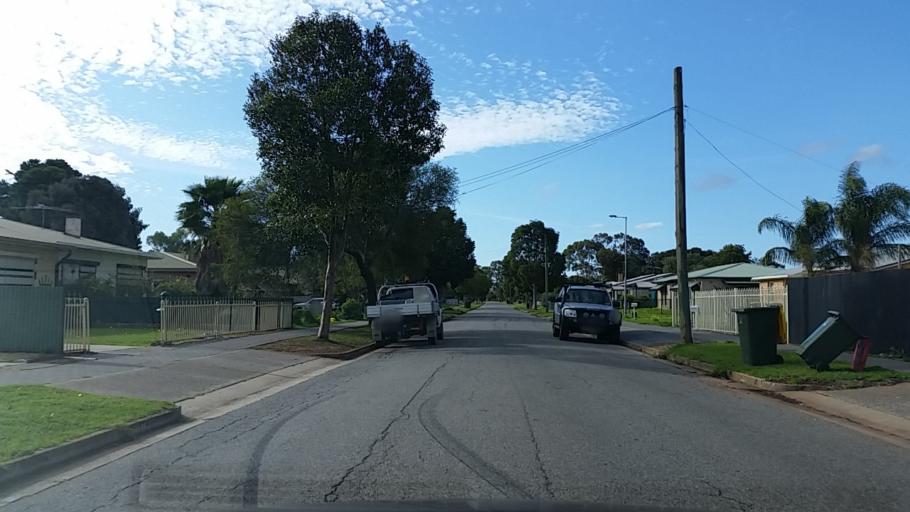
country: AU
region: South Australia
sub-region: Salisbury
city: Elizabeth
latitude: -34.7321
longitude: 138.6653
